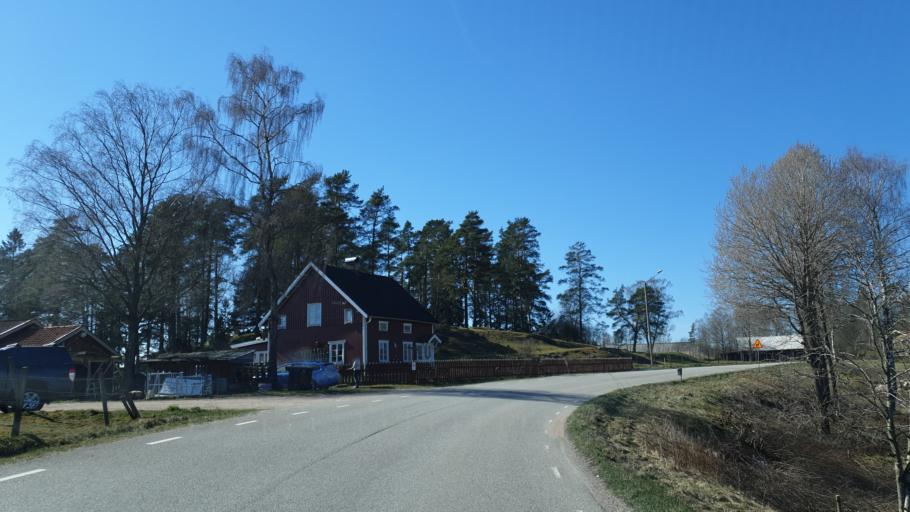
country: SE
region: Vaestra Goetaland
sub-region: Svenljunga Kommun
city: Svenljunga
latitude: 57.4394
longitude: 13.1283
